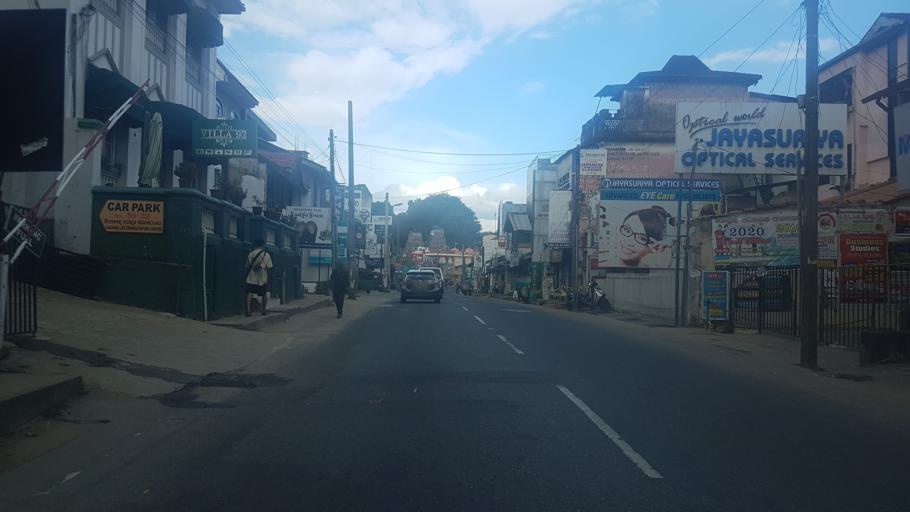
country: LK
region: Central
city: Kandy
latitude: 7.2912
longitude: 80.6312
